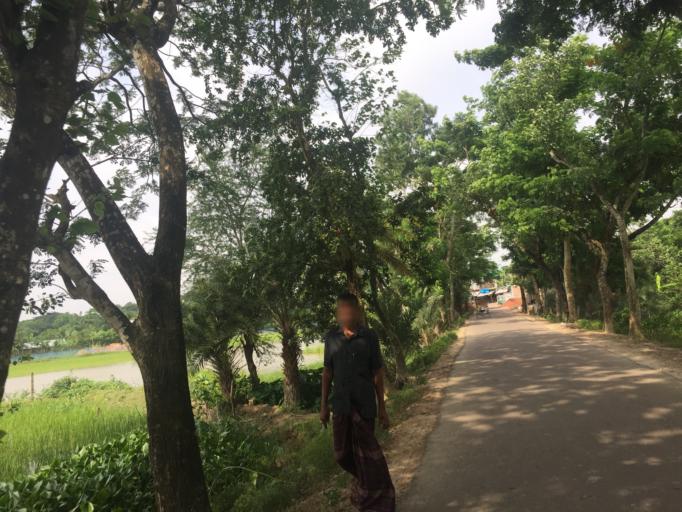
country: BD
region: Barisal
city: Mathba
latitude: 22.2145
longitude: 89.9140
